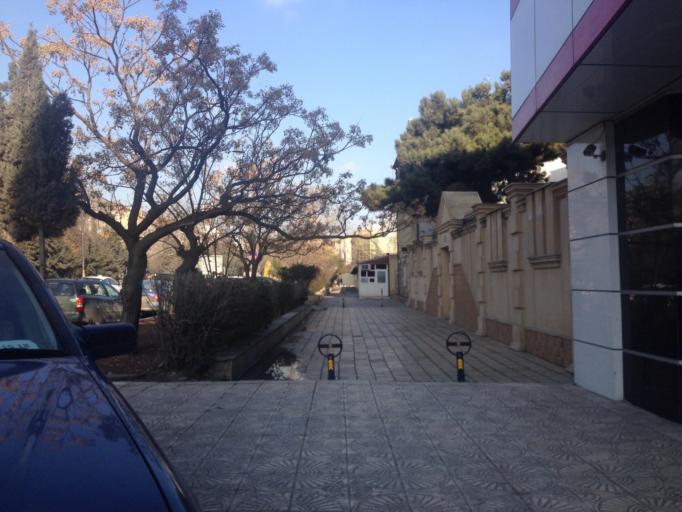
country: AZ
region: Baki
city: Baku
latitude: 40.4086
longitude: 49.8486
